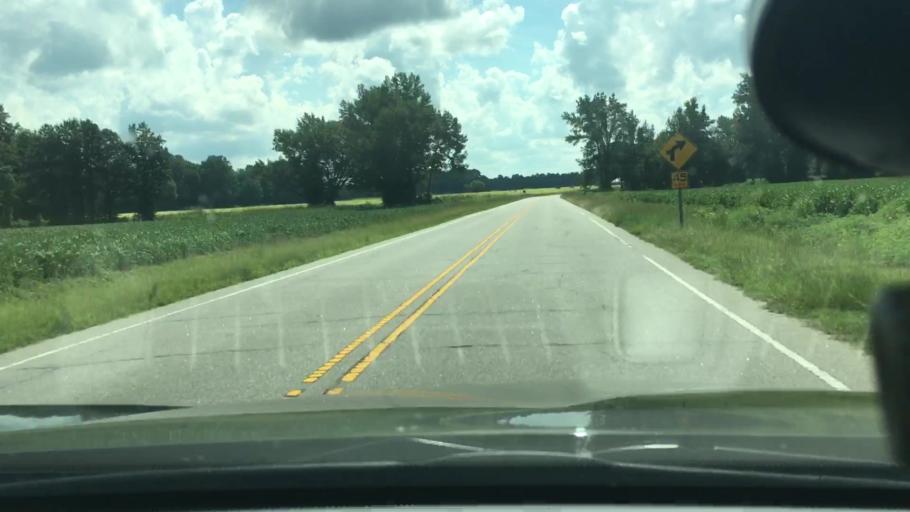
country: US
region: North Carolina
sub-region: Edgecombe County
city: Pinetops
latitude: 35.7552
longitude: -77.5491
